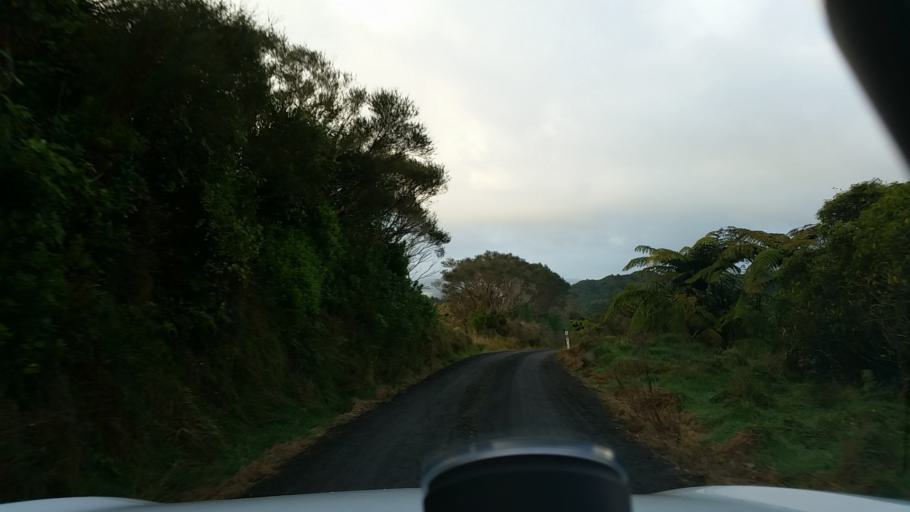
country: NZ
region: Taranaki
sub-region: South Taranaki District
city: Eltham
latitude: -39.4399
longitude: 174.4501
